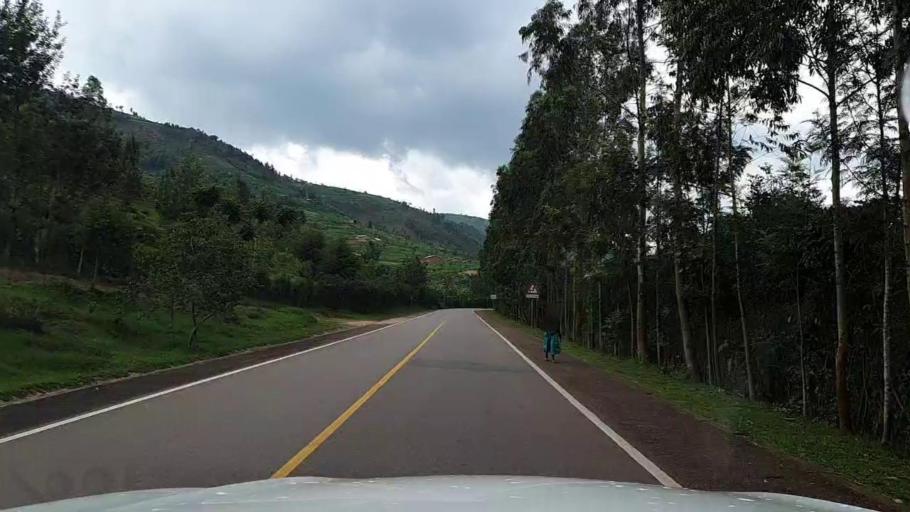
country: RW
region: Northern Province
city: Byumba
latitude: -1.6813
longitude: 30.1034
